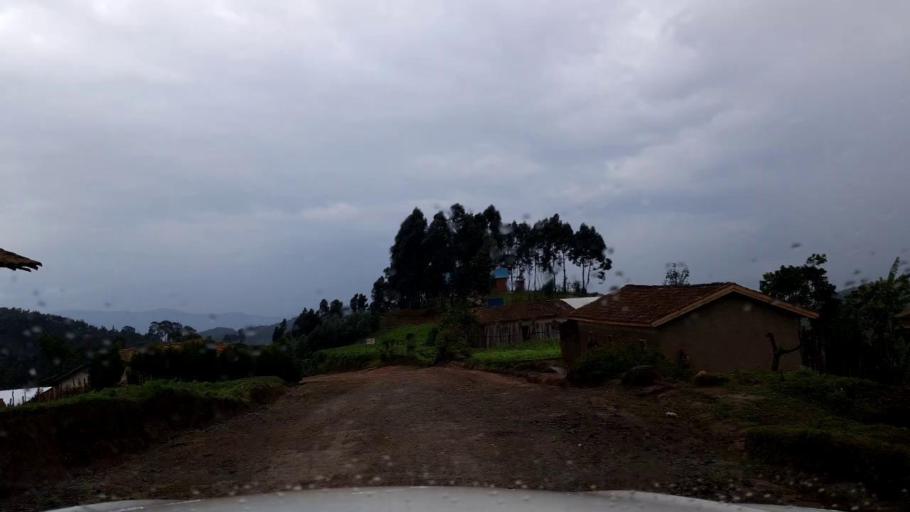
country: RW
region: Western Province
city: Kibuye
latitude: -2.0150
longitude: 29.4677
